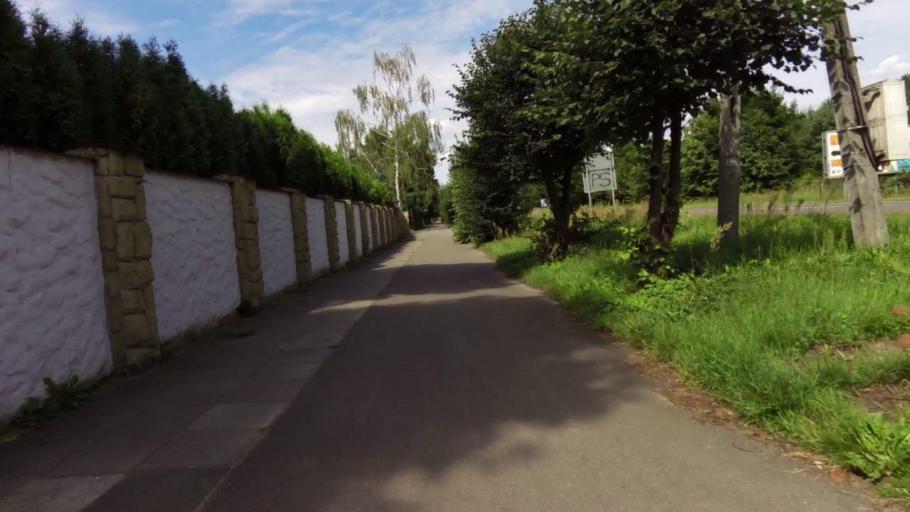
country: PL
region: West Pomeranian Voivodeship
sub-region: Powiat stargardzki
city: Kobylanka
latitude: 53.3519
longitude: 14.9248
